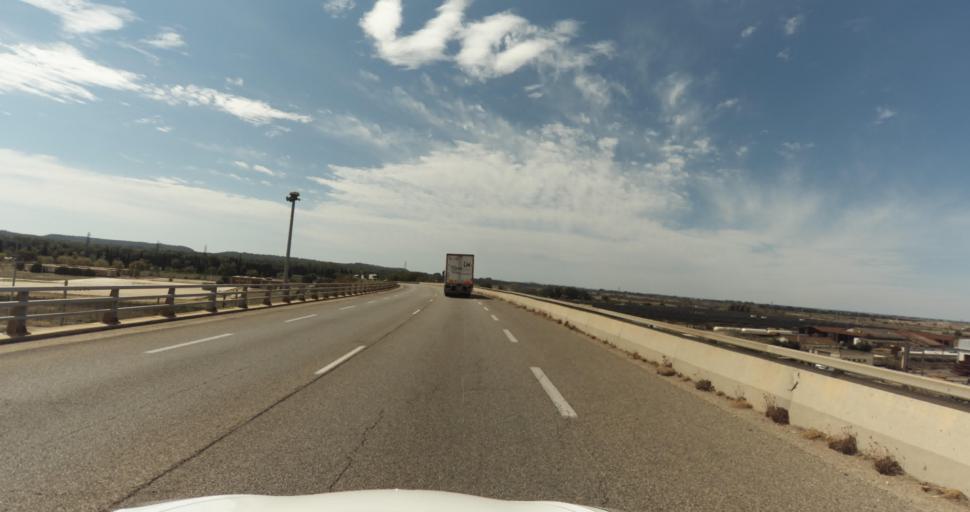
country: FR
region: Provence-Alpes-Cote d'Azur
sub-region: Departement des Bouches-du-Rhone
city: Miramas
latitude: 43.5816
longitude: 4.9848
